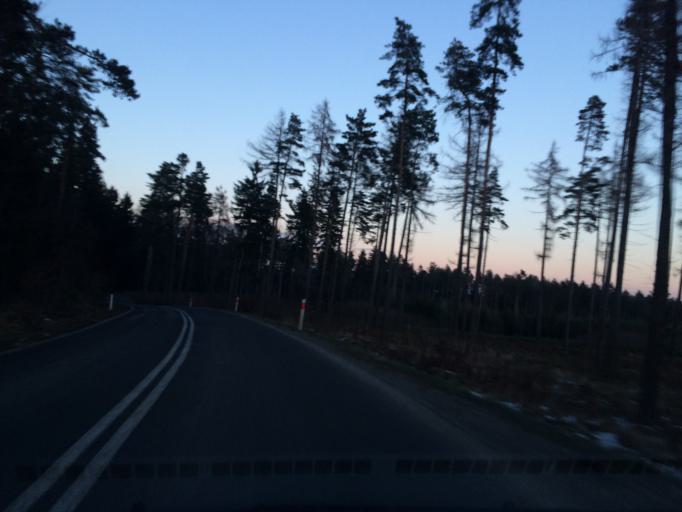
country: PL
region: Lower Silesian Voivodeship
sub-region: Powiat lwowecki
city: Wlen
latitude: 51.1211
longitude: 15.7221
